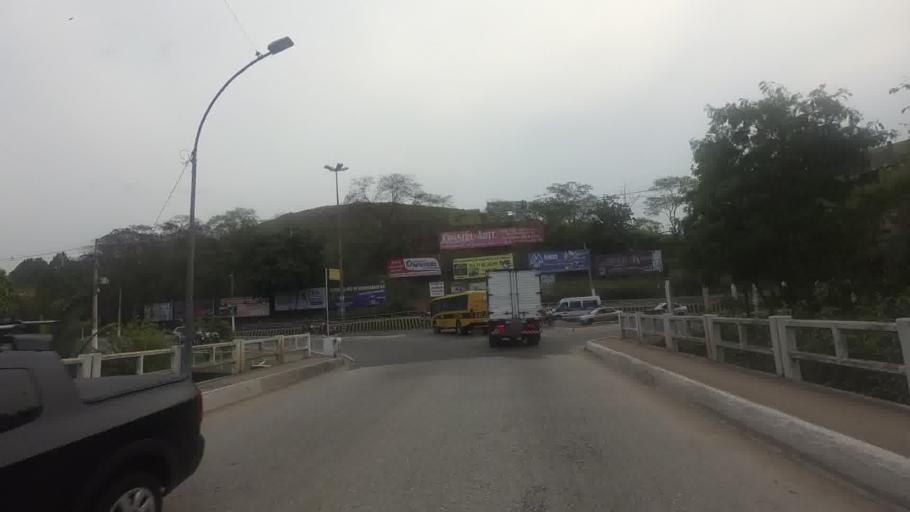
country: BR
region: Rio de Janeiro
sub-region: Santo Antonio De Padua
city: Santo Antonio de Padua
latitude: -21.5495
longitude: -42.1776
